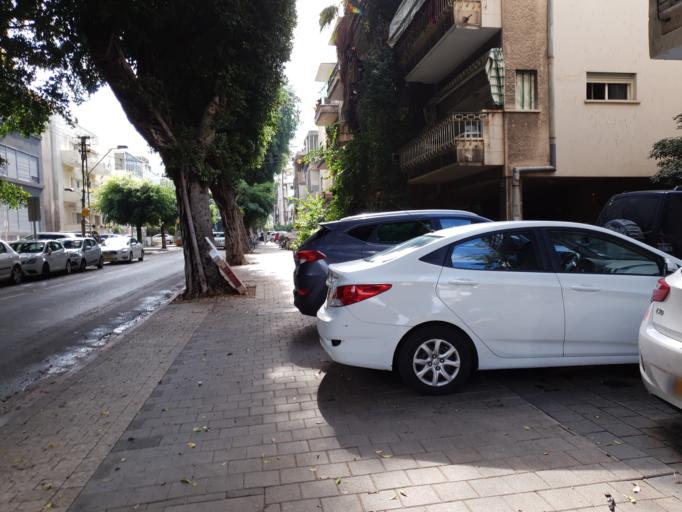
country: IL
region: Tel Aviv
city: Tel Aviv
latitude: 32.0824
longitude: 34.7759
